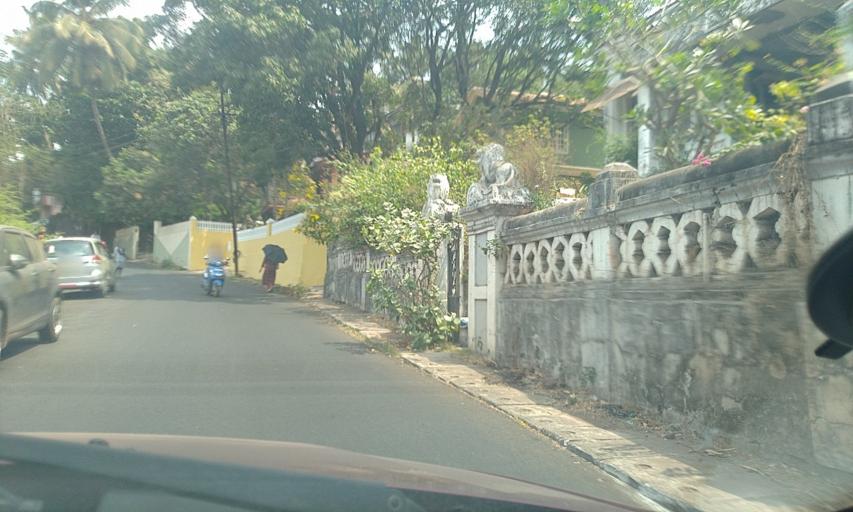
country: IN
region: Goa
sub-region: North Goa
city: Mapuca
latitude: 15.5937
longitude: 73.8106
